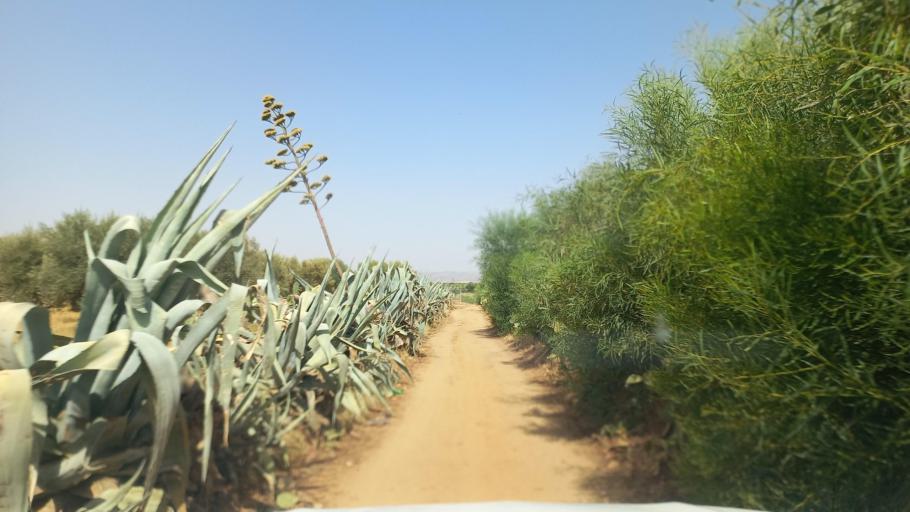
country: TN
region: Al Qasrayn
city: Kasserine
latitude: 35.2389
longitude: 9.0508
